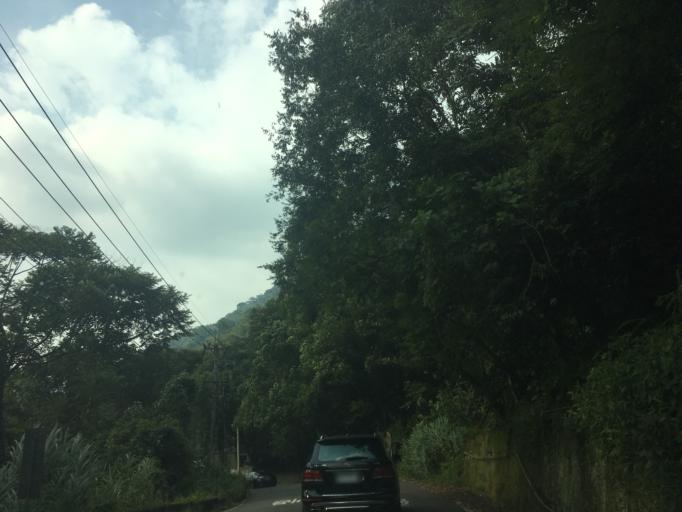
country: TW
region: Taiwan
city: Fengyuan
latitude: 24.3042
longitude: 120.9244
